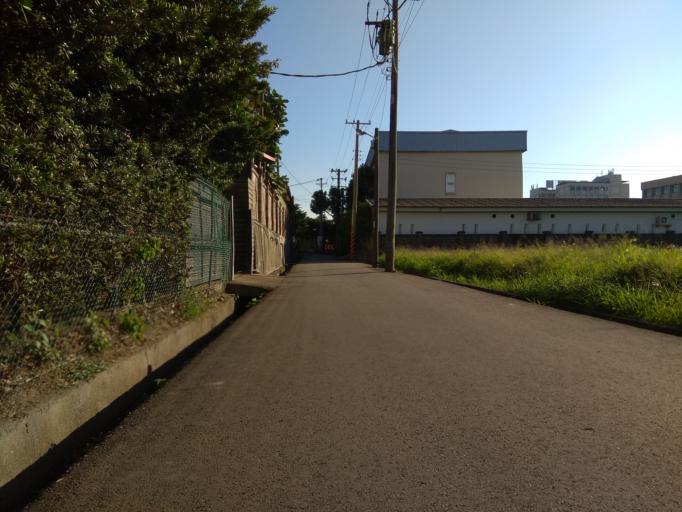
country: TW
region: Taiwan
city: Taoyuan City
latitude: 24.9927
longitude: 121.2325
